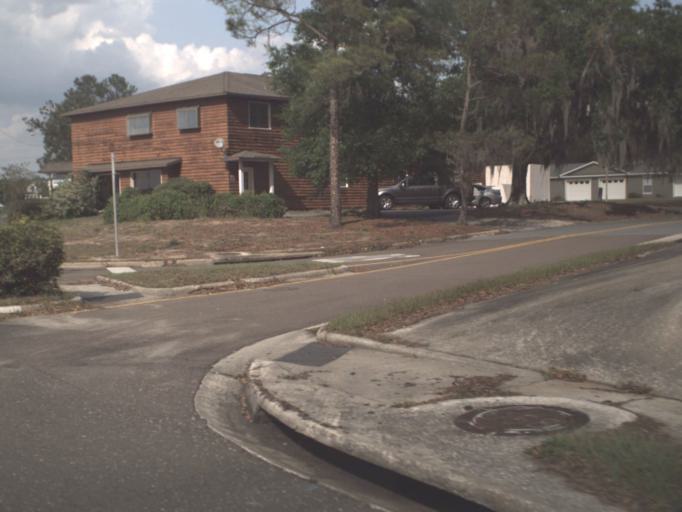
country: US
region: Florida
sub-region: Lake County
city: Eustis
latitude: 28.8446
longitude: -81.6854
